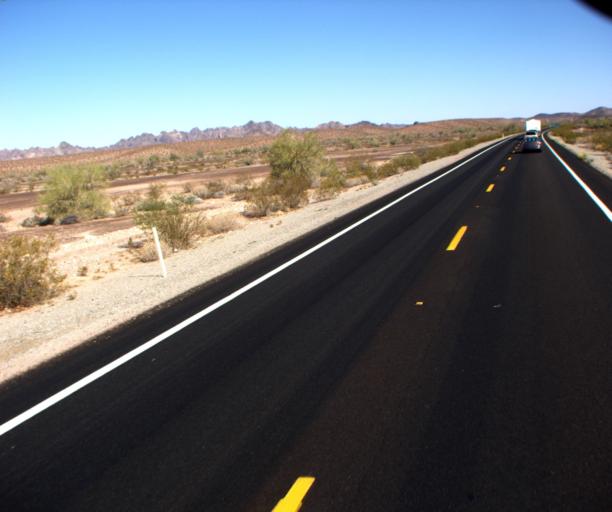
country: US
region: Arizona
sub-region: La Paz County
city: Quartzsite
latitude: 33.1819
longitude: -114.2755
